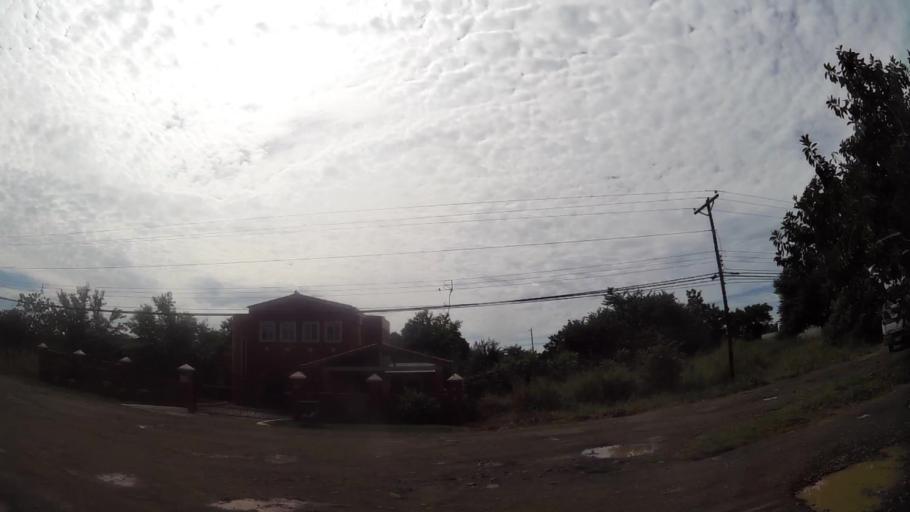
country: PA
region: Panama
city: Nueva Gorgona
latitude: 8.5458
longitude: -79.8964
